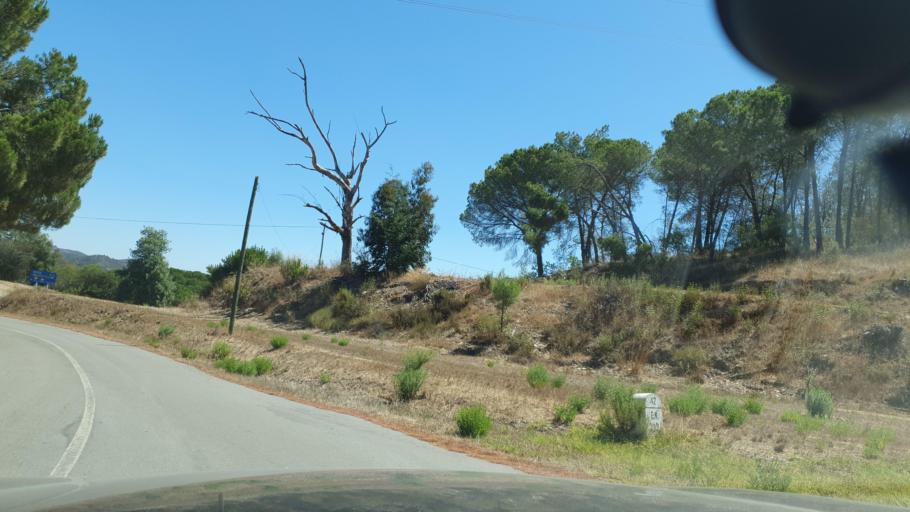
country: PT
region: Faro
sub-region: Monchique
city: Monchique
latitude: 37.5056
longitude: -8.4365
